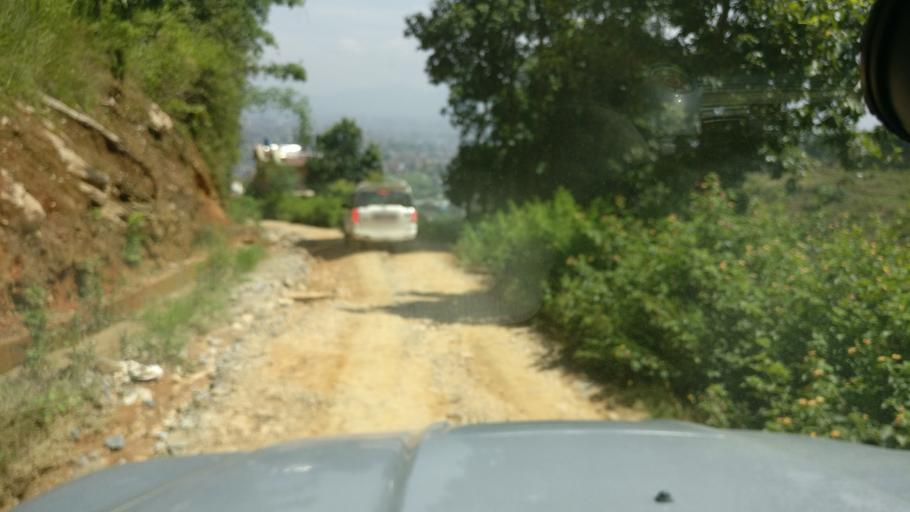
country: NP
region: Central Region
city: Kirtipur
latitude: 27.7029
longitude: 85.2553
